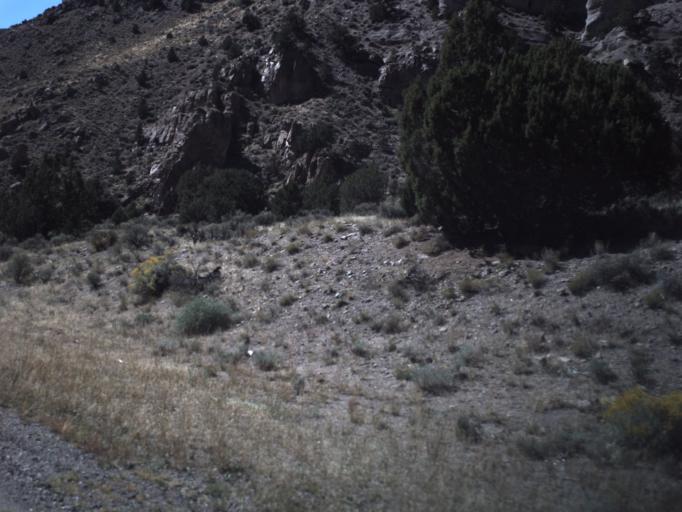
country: US
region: Utah
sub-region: Piute County
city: Junction
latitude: 38.1963
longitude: -112.1263
